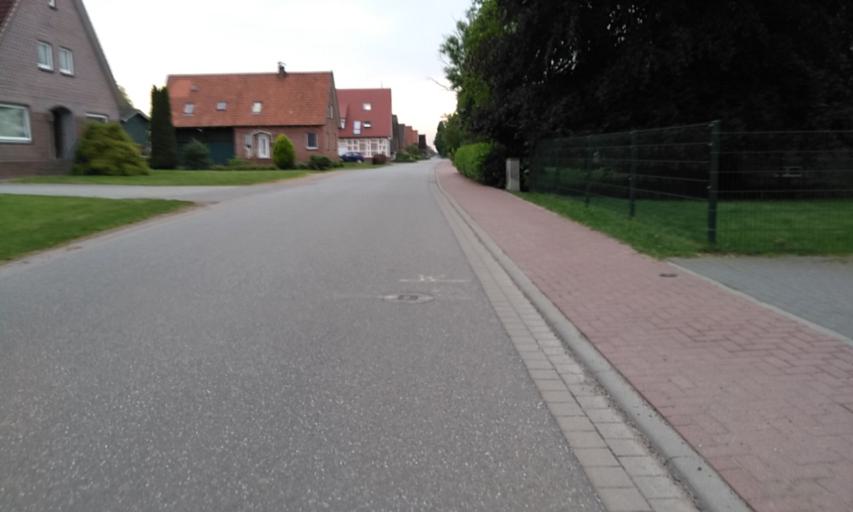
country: DE
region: Lower Saxony
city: Jork
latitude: 53.5172
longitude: 9.6762
